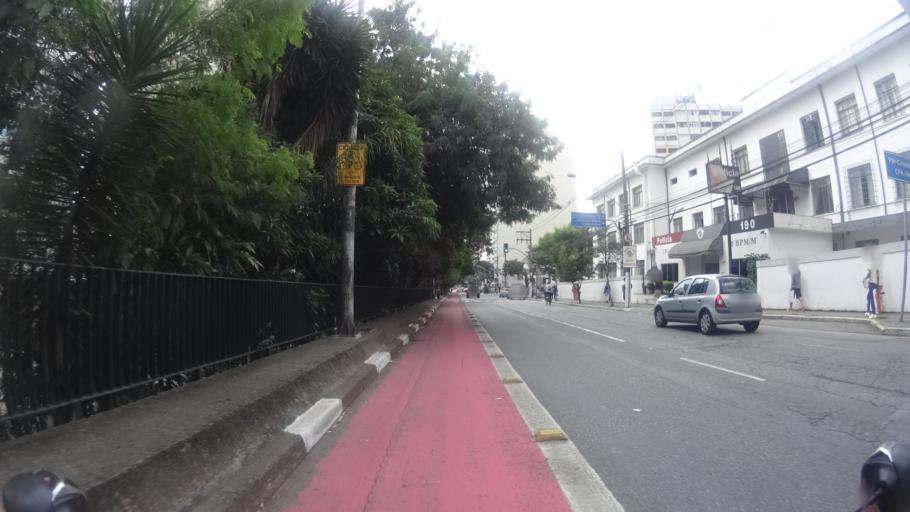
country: BR
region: Sao Paulo
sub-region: Sao Paulo
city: Sao Paulo
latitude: -23.5655
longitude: -46.6393
